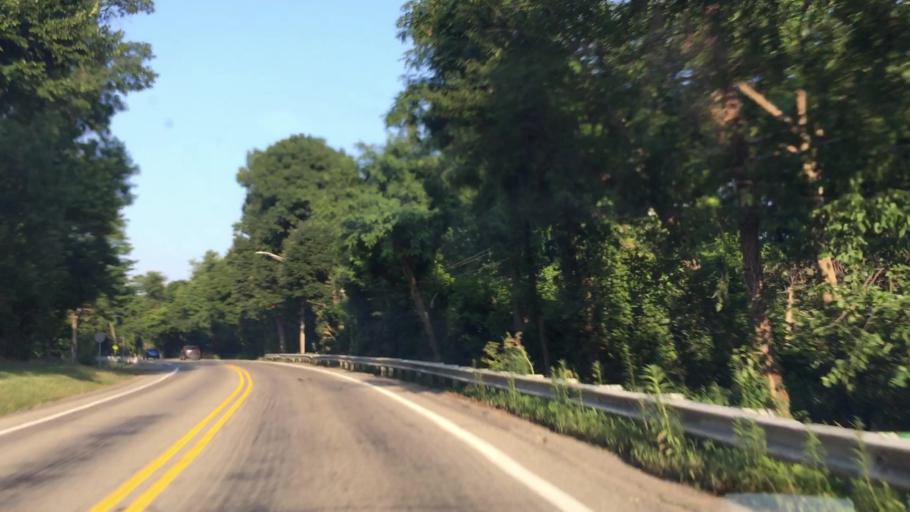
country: US
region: Pennsylvania
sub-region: Allegheny County
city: Bryn Mawr
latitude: 40.3152
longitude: -80.1003
